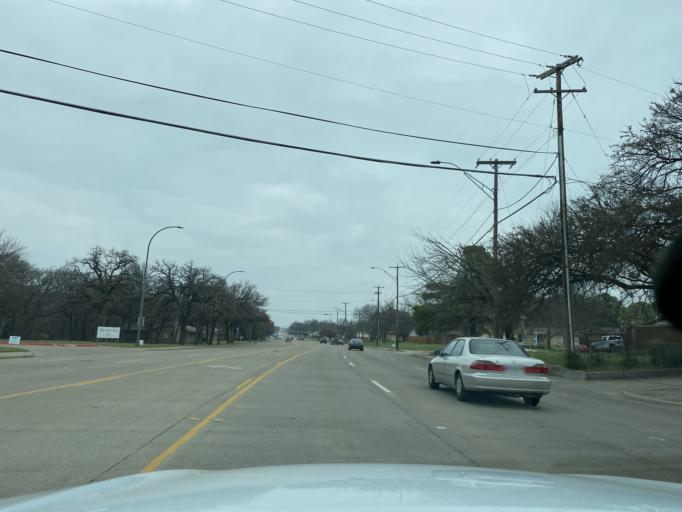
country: US
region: Texas
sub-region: Tarrant County
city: Arlington
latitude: 32.7245
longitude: -97.0974
